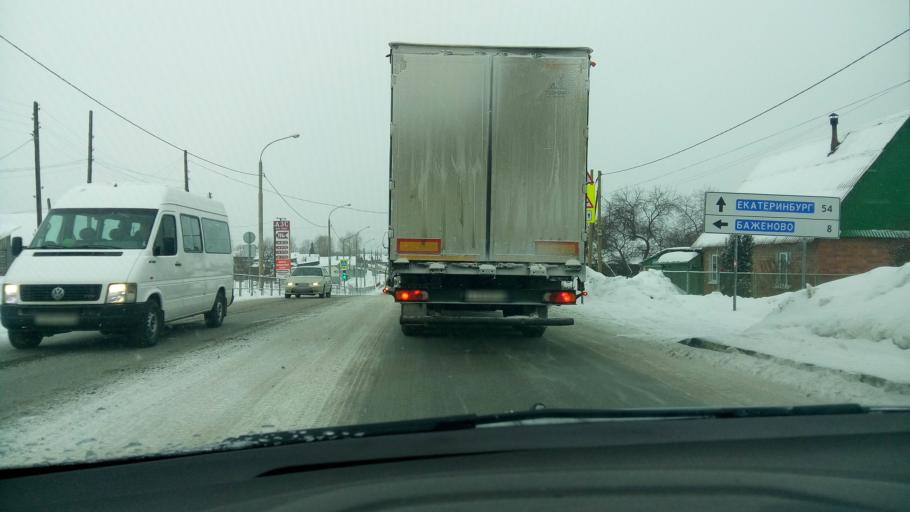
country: RU
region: Sverdlovsk
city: Beloyarskiy
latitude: 56.7567
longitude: 61.3939
